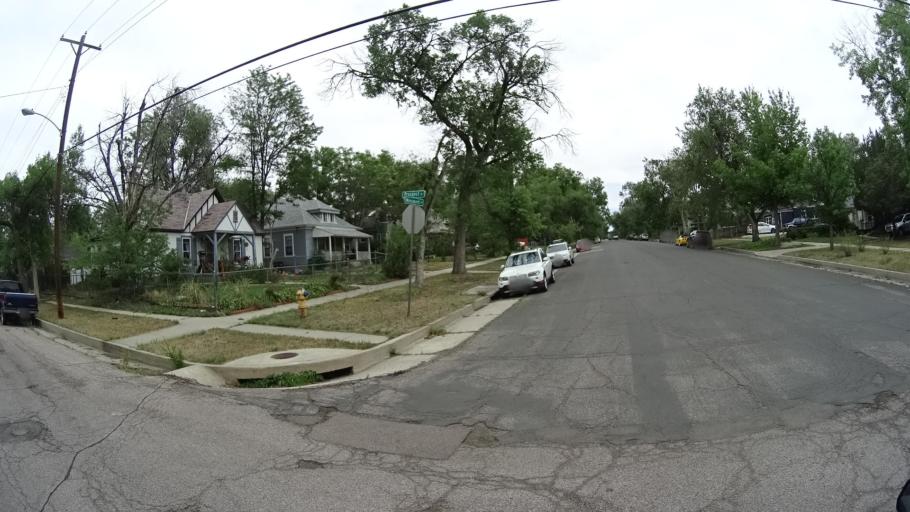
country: US
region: Colorado
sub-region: El Paso County
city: Colorado Springs
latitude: 38.8434
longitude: -104.8103
